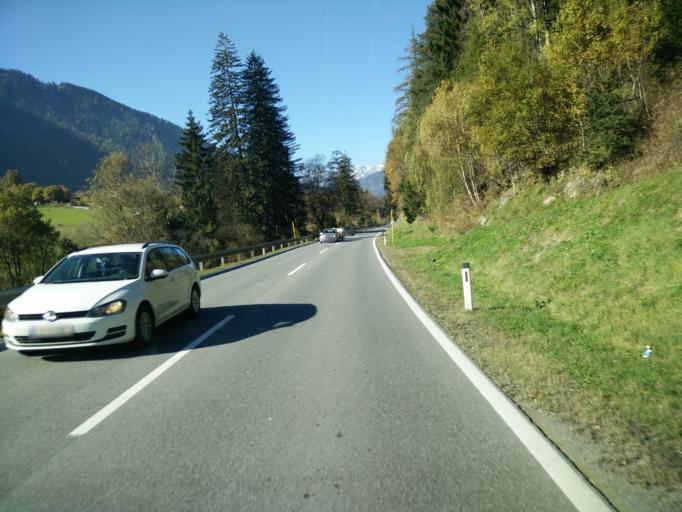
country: AT
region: Tyrol
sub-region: Politischer Bezirk Imst
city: Sautens
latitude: 47.2071
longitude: 10.8785
